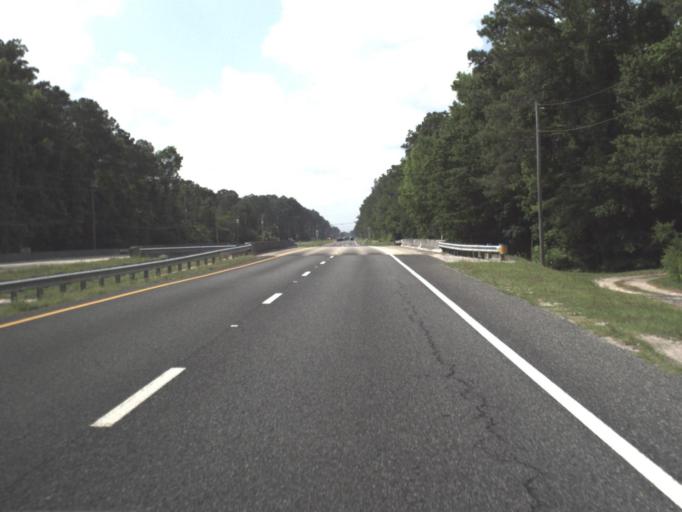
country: US
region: Florida
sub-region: Saint Johns County
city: Saint Augustine Shores
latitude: 29.7754
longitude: -81.3162
